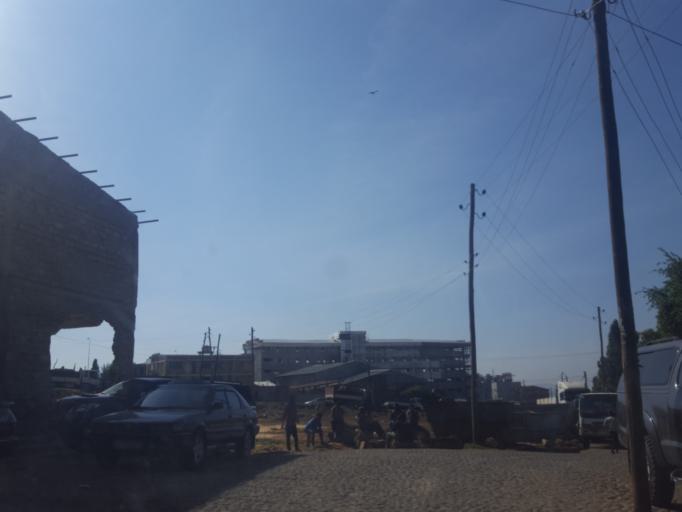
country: ET
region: Adis Abeba
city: Addis Ababa
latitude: 9.0601
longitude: 38.7134
